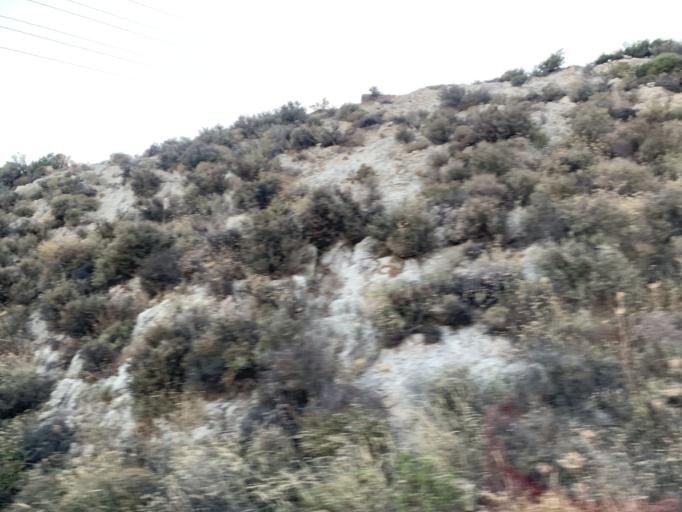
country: TR
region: Izmir
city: Alacati
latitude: 38.2840
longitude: 26.4027
